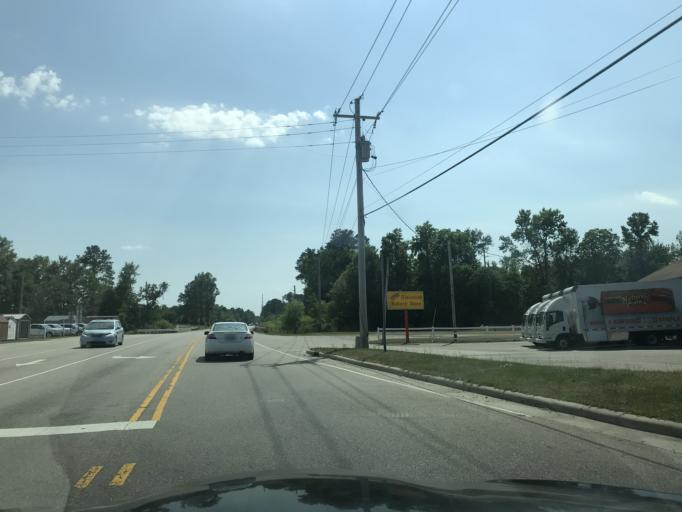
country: US
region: North Carolina
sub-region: Wilson County
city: Wilson
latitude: 35.7076
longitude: -77.9518
